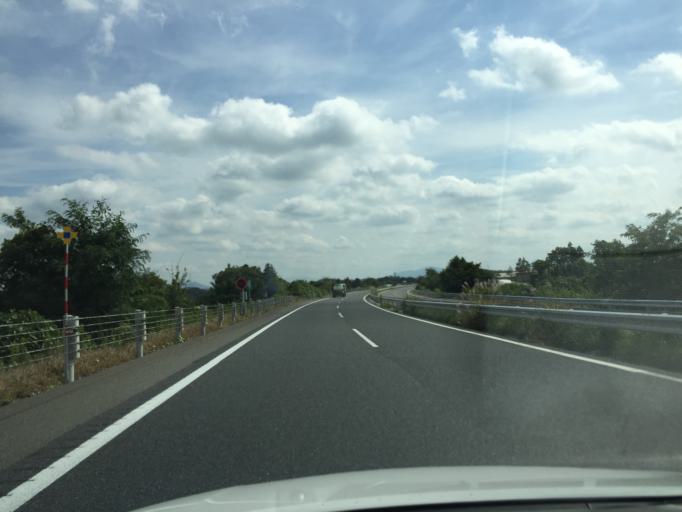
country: JP
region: Fukushima
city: Koriyama
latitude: 37.4559
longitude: 140.3976
